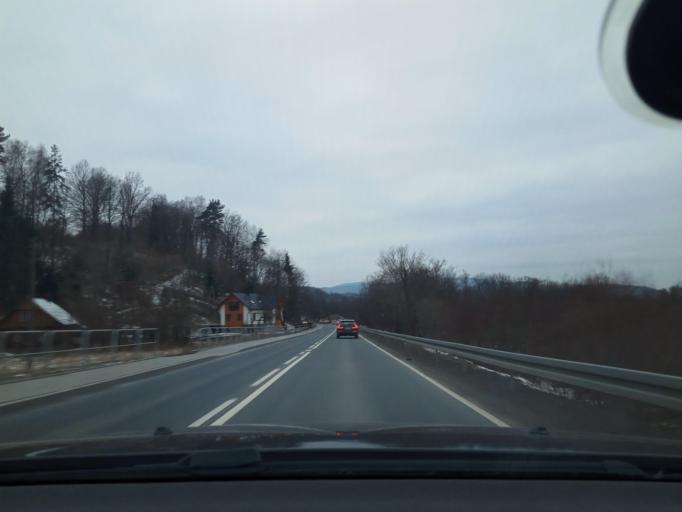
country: PL
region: Lesser Poland Voivodeship
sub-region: Powiat myslenicki
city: Lubien
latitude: 49.7169
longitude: 19.9907
